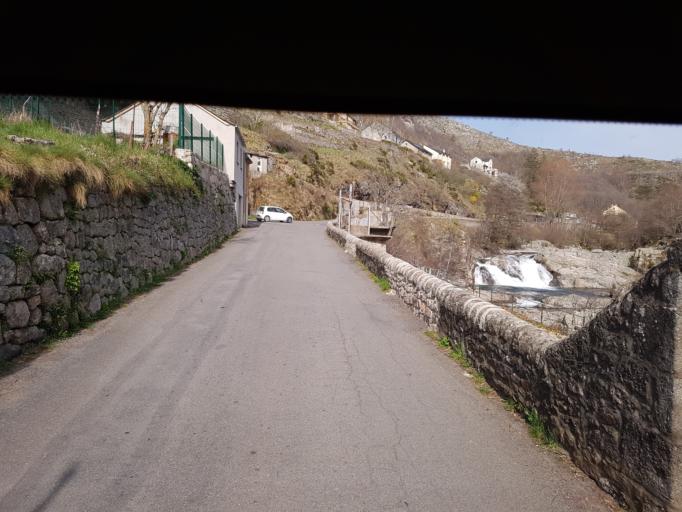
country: FR
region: Languedoc-Roussillon
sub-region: Departement de la Lozere
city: Florac
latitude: 44.3631
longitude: 3.7464
